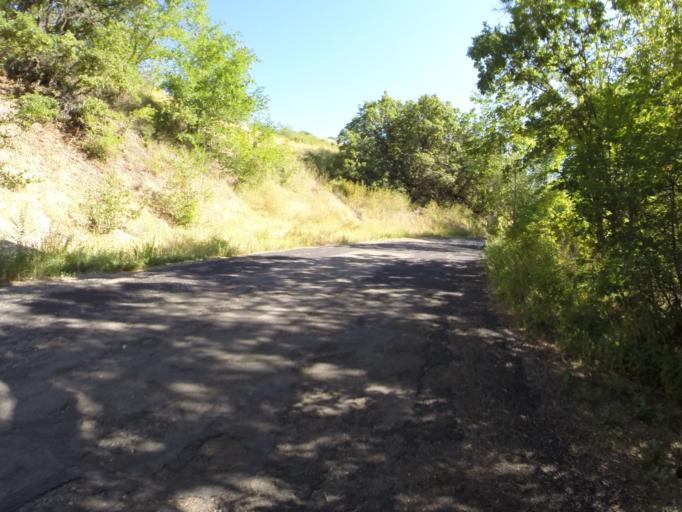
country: US
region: Utah
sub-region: Salt Lake County
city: Salt Lake City
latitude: 40.7865
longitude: -111.8826
